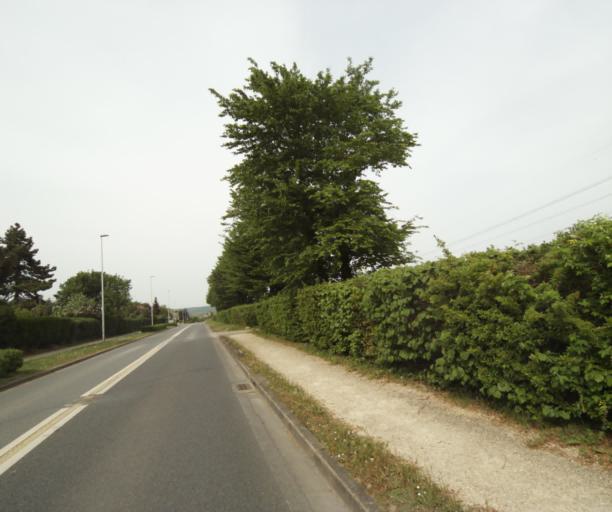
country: FR
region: Ile-de-France
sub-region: Departement de Seine-et-Marne
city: Torcy
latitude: 48.8510
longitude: 2.6582
